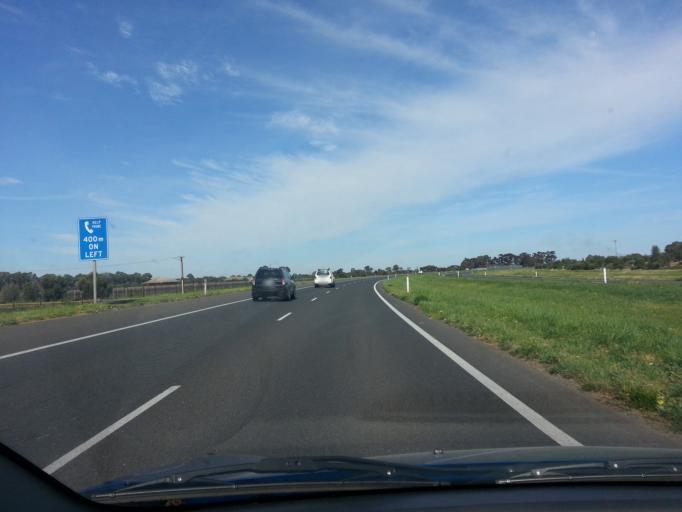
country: AU
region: South Australia
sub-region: Playford
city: Smithfield
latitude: -34.6753
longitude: 138.6502
